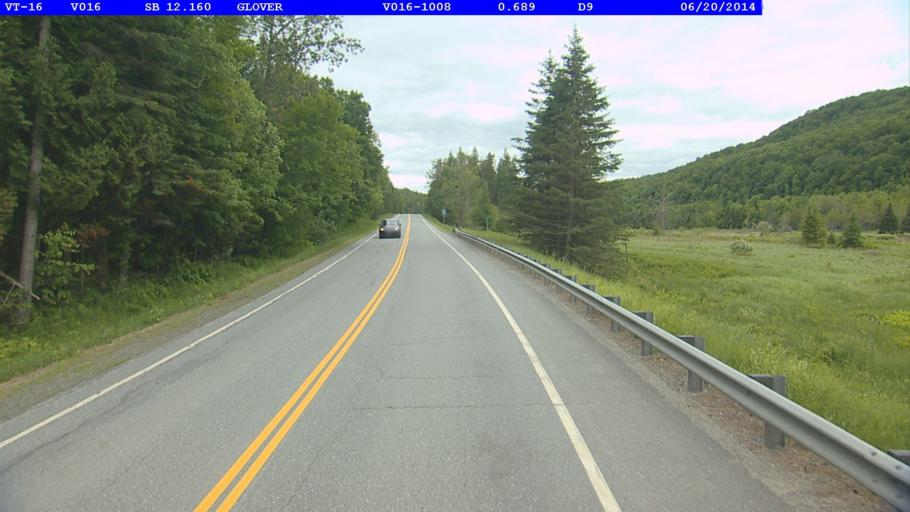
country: US
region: Vermont
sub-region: Caledonia County
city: Hardwick
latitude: 44.6376
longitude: -72.2106
